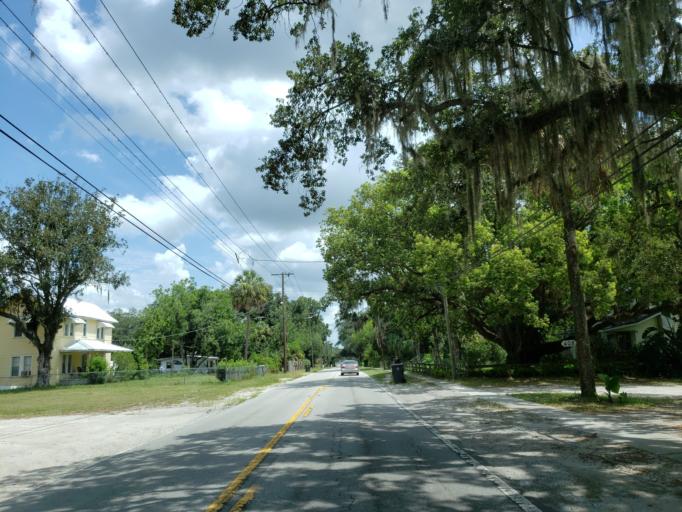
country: US
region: Florida
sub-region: Hillsborough County
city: Seffner
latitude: 27.9914
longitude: -82.2777
